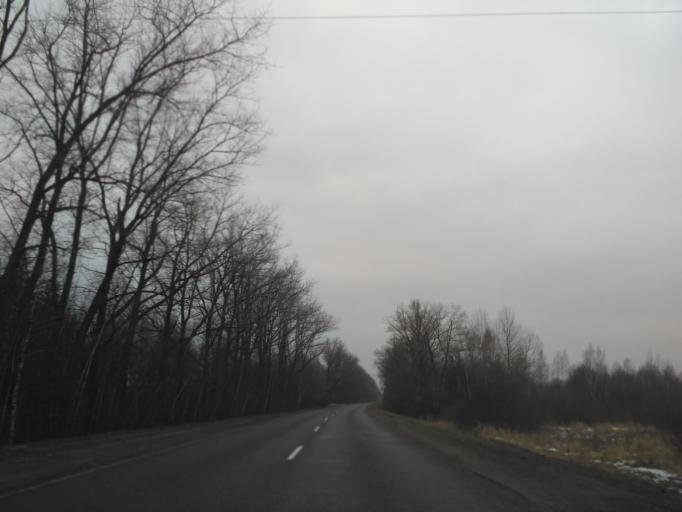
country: BY
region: Minsk
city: Snow
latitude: 53.2659
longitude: 26.3282
